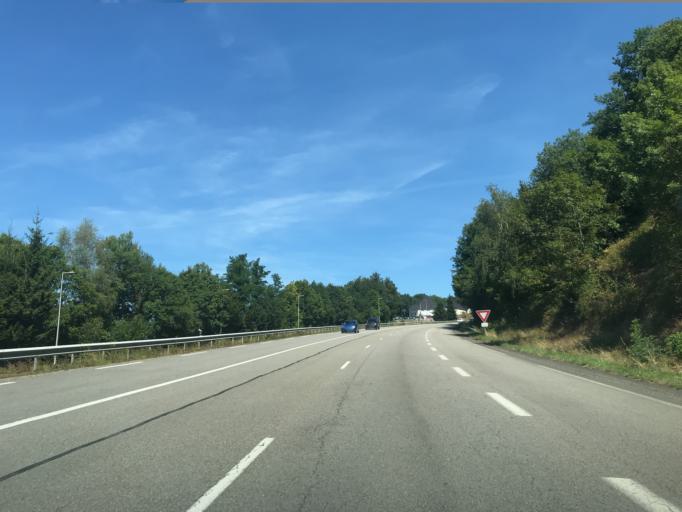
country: FR
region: Limousin
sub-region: Departement de la Correze
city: Tulle
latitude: 45.2757
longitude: 1.7889
